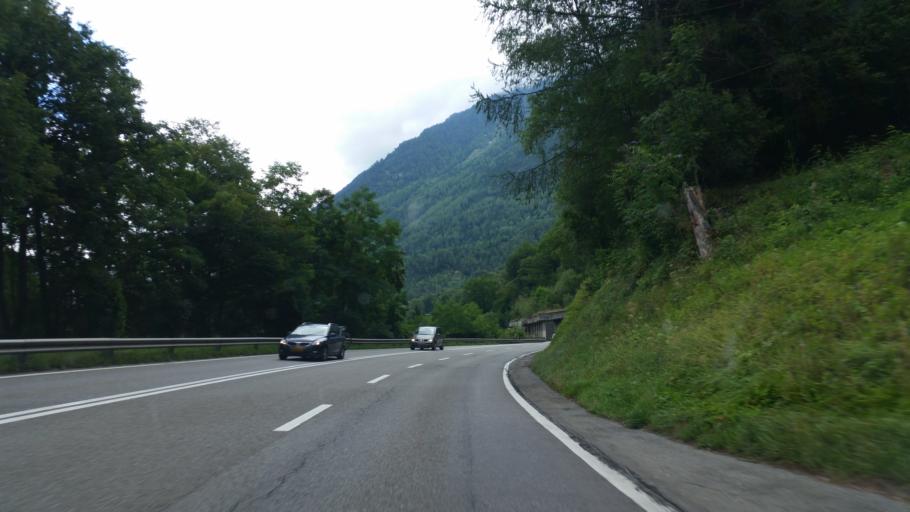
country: CH
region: Valais
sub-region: Martigny District
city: Martigny-Combe
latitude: 46.0733
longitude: 7.0562
